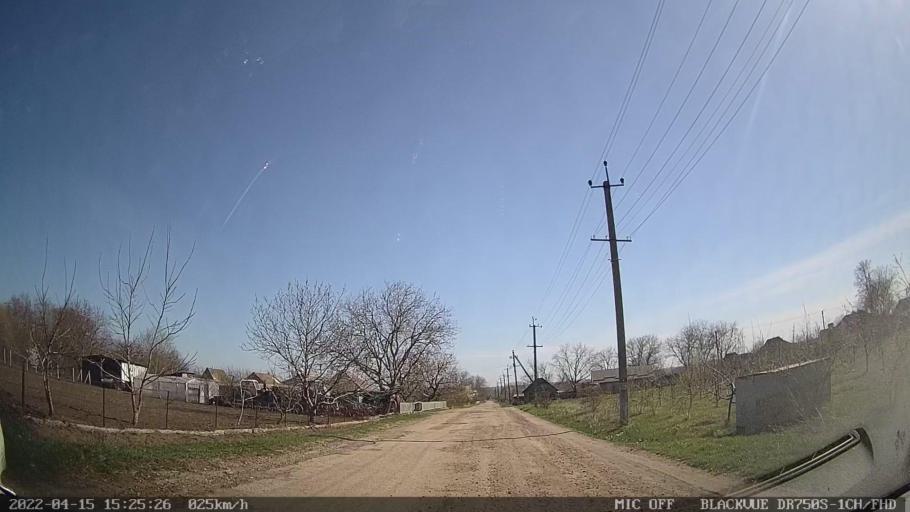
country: MD
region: Raionul Ocnita
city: Otaci
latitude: 48.3651
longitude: 27.9263
